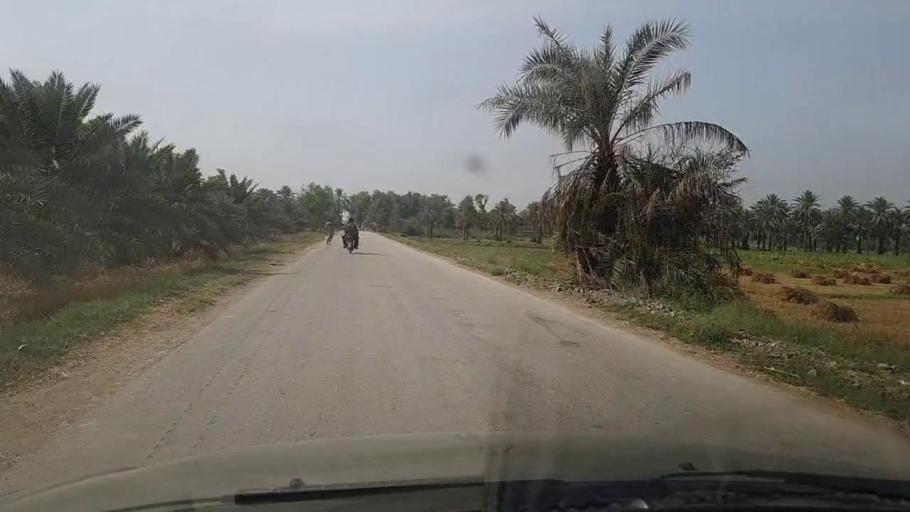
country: PK
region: Sindh
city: Gambat
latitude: 27.4537
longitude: 68.4861
